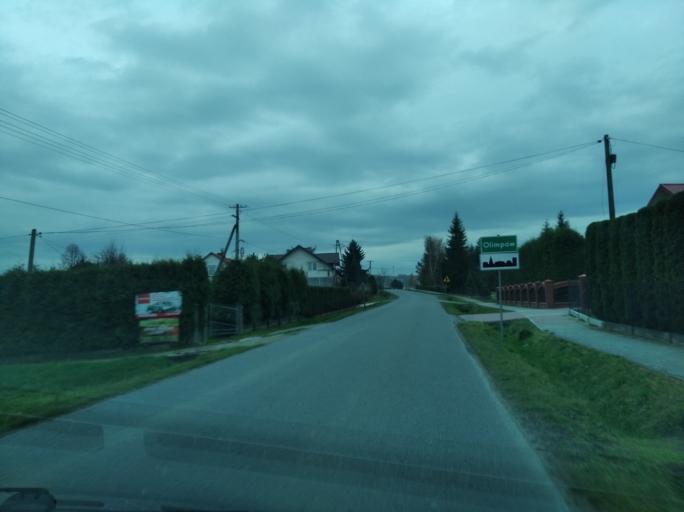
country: PL
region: Subcarpathian Voivodeship
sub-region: Powiat ropczycko-sedziszowski
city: Iwierzyce
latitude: 50.0076
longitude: 21.7555
